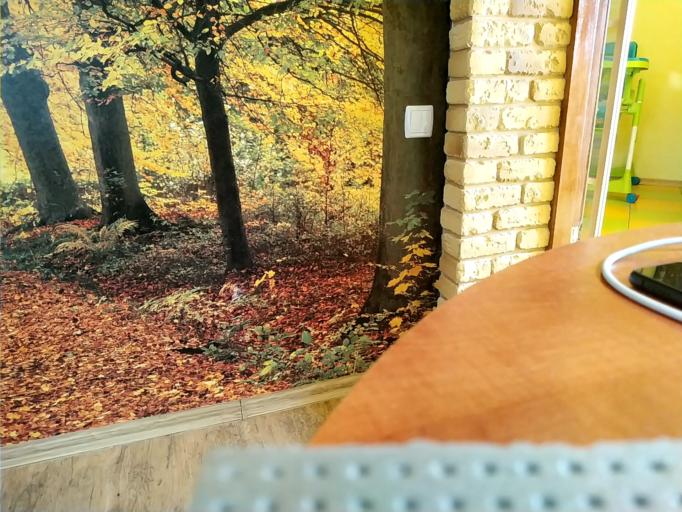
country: RU
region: Tverskaya
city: Kalashnikovo
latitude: 57.3484
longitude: 35.2011
